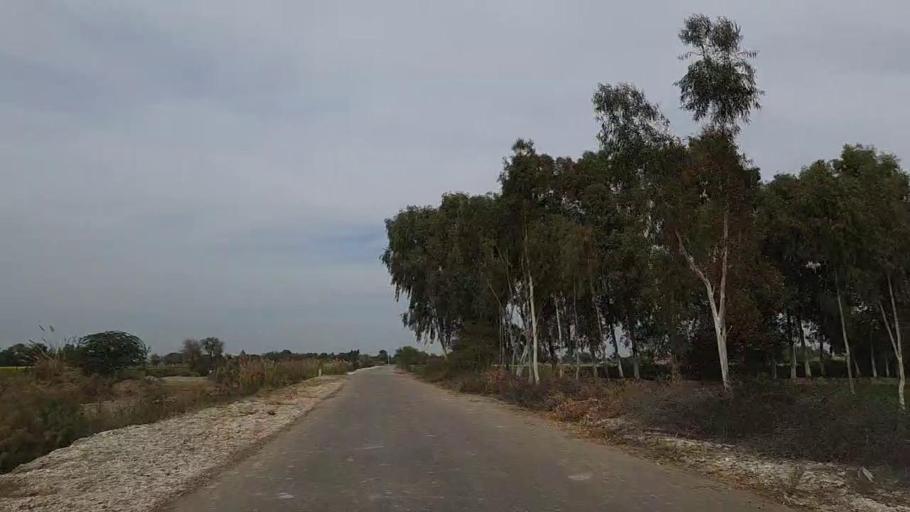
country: PK
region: Sindh
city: Daur
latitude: 26.4256
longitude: 68.4809
